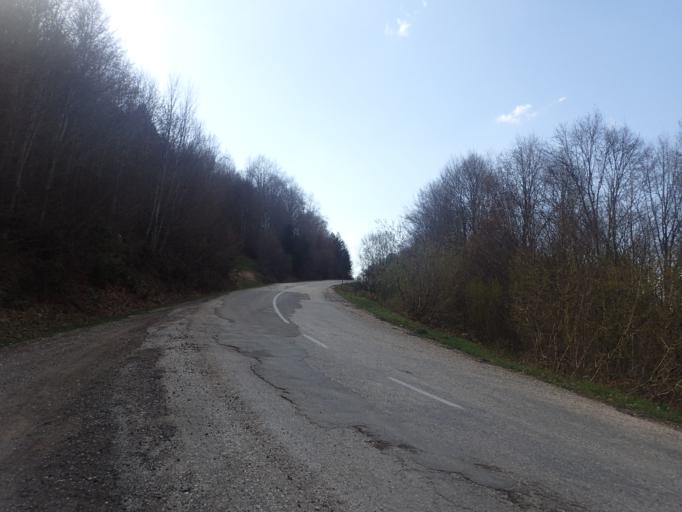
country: TR
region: Sivas
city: Koyulhisar
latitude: 40.3558
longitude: 37.8353
